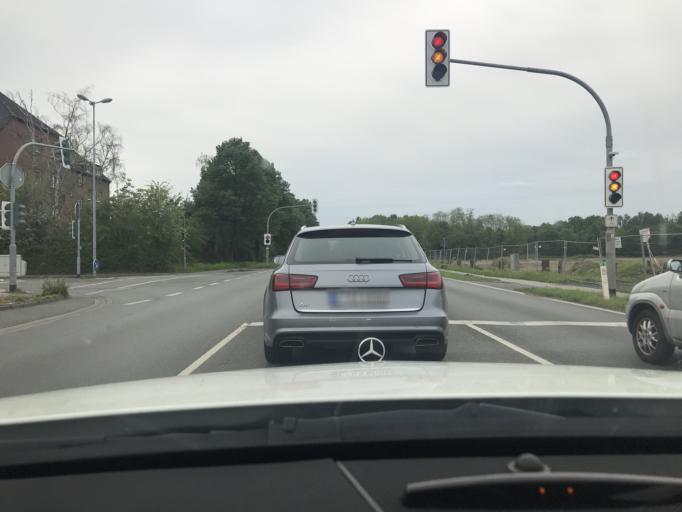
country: DE
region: North Rhine-Westphalia
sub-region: Regierungsbezirk Dusseldorf
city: Moers
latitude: 51.4704
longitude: 6.6315
